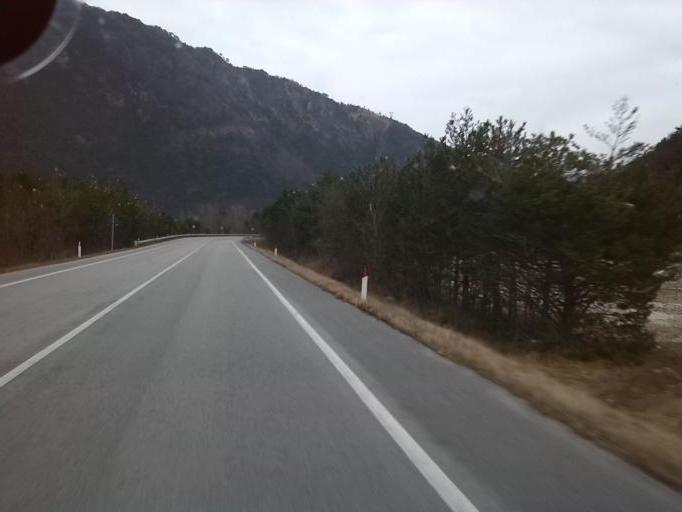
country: IT
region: Friuli Venezia Giulia
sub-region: Provincia di Udine
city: Amaro
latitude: 46.3858
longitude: 13.1386
